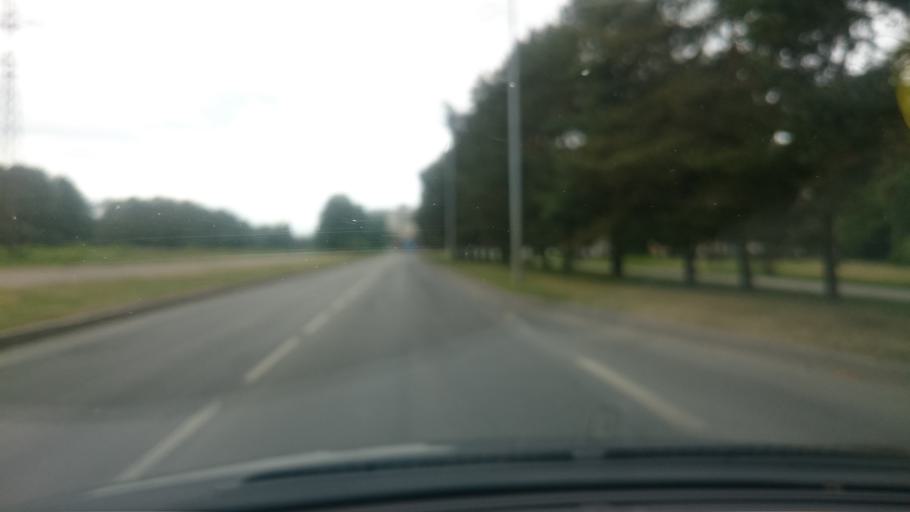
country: EE
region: Harju
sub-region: Saue vald
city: Laagri
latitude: 59.4071
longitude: 24.6392
